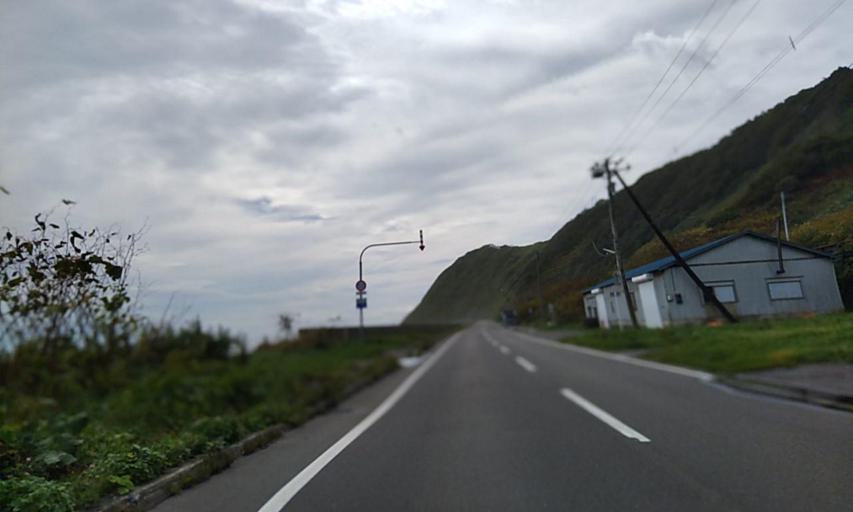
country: JP
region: Hokkaido
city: Kushiro
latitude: 42.7964
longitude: 143.8071
